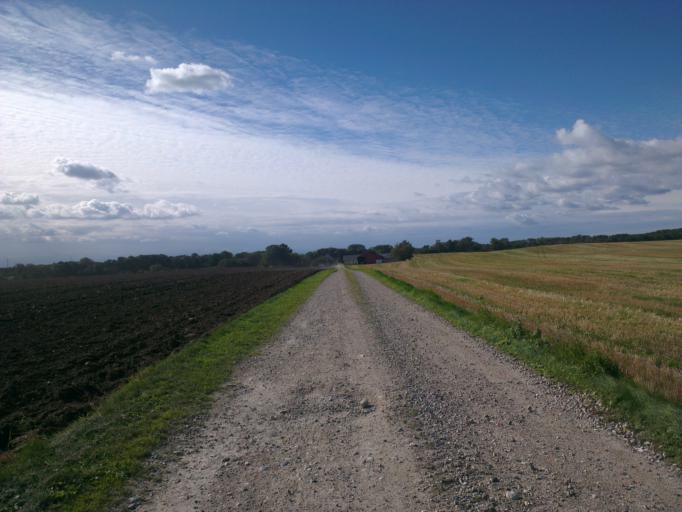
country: DK
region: Capital Region
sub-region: Frederikssund Kommune
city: Jaegerspris
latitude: 55.8177
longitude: 11.9823
